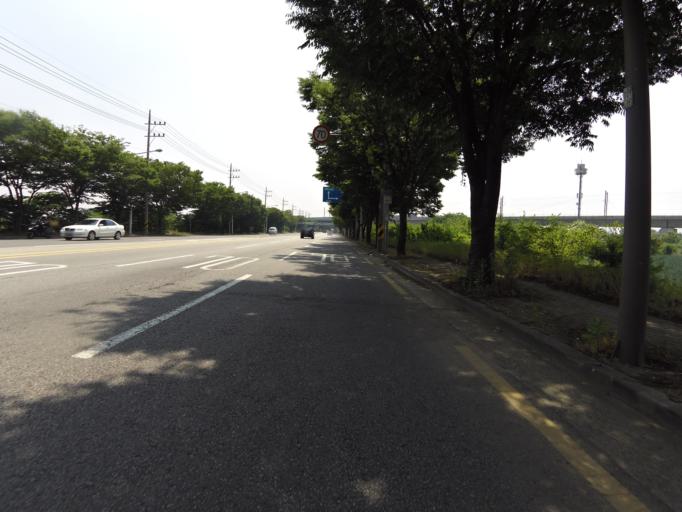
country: KR
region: Gyeongsangbuk-do
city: Gyeongsan-si
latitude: 35.8553
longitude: 128.7225
